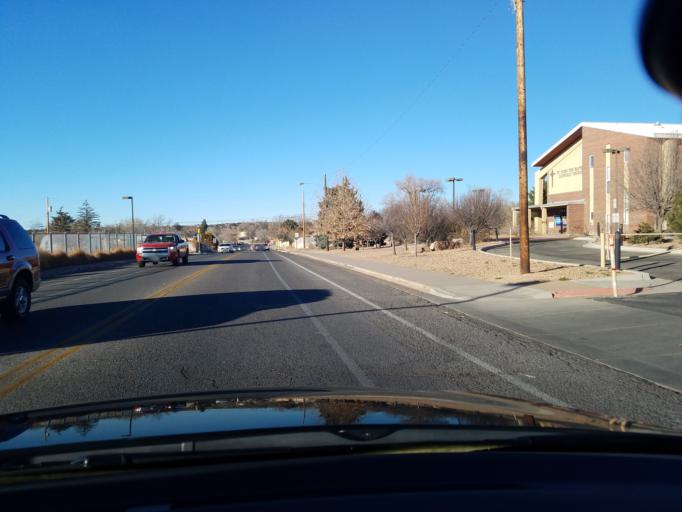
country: US
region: New Mexico
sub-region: Santa Fe County
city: Agua Fria
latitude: 35.6642
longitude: -105.9777
